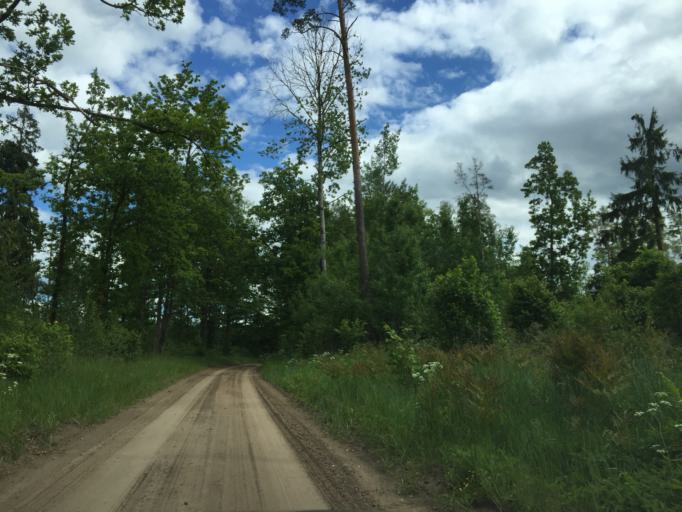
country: LV
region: Lecava
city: Iecava
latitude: 56.5723
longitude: 24.2937
